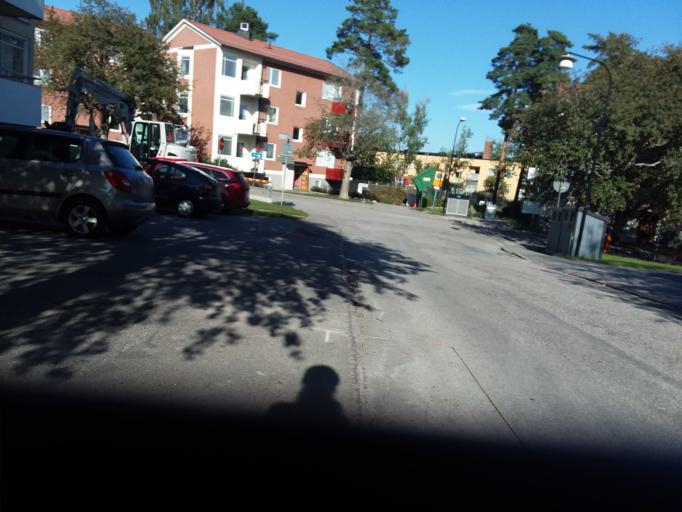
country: SE
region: Stockholm
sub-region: Stockholms Kommun
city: Bromma
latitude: 59.3497
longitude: 17.8797
